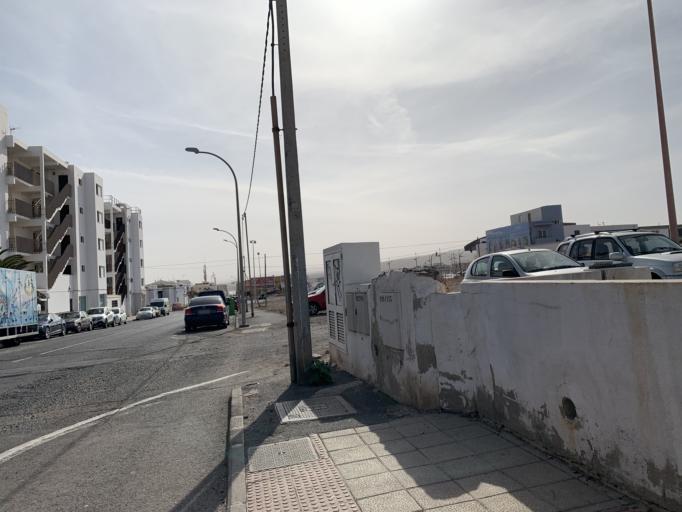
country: ES
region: Canary Islands
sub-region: Provincia de Las Palmas
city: Puerto del Rosario
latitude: 28.5048
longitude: -13.8583
